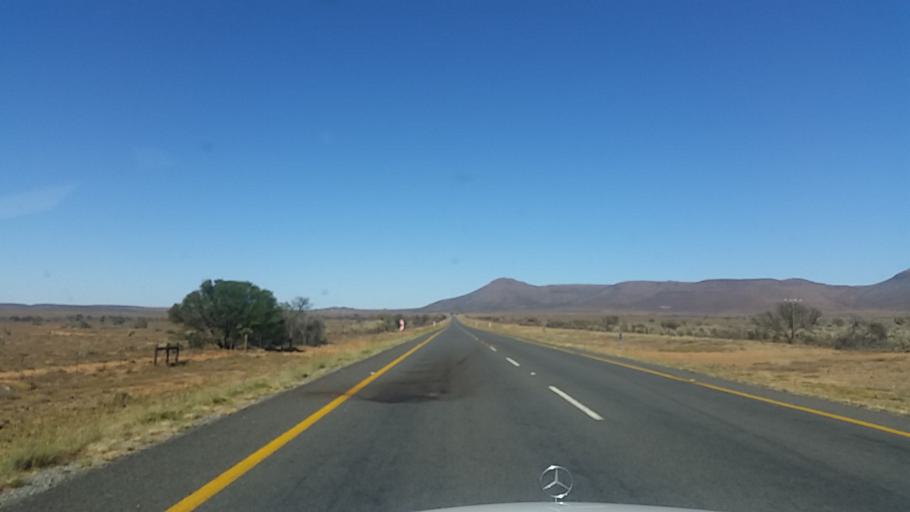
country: ZA
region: Eastern Cape
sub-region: Cacadu District Municipality
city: Graaff-Reinet
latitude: -32.0074
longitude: 24.6572
